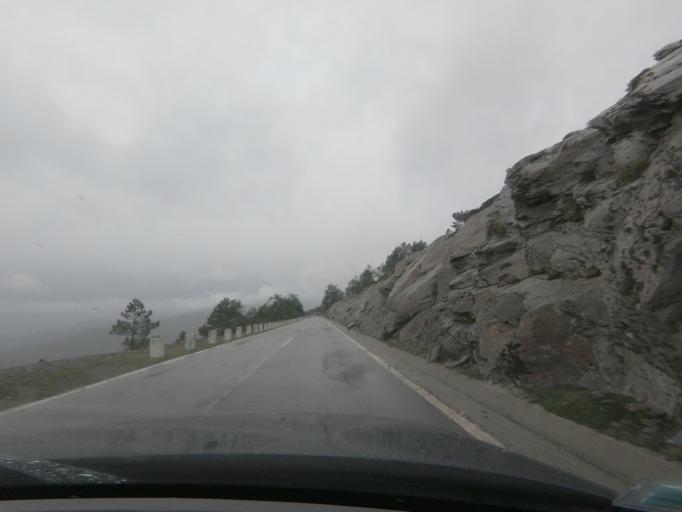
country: PT
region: Vila Real
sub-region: Mondim de Basto
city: Mondim de Basto
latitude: 41.3350
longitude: -7.8767
